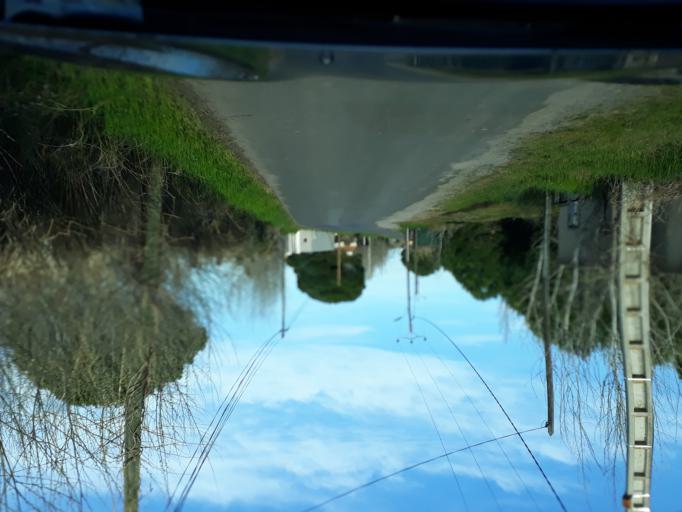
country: FR
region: Languedoc-Roussillon
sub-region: Departement de l'Herault
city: Marseillan
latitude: 43.3295
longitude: 3.5506
